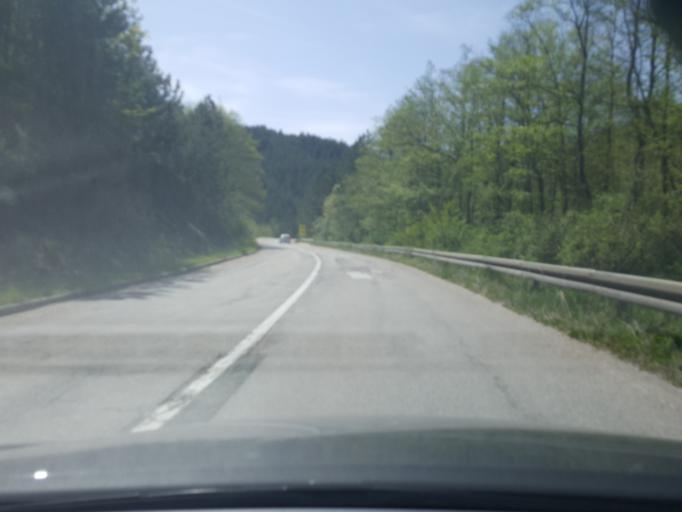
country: RS
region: Central Serbia
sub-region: Zlatiborski Okrug
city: Cajetina
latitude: 43.7862
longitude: 19.6695
